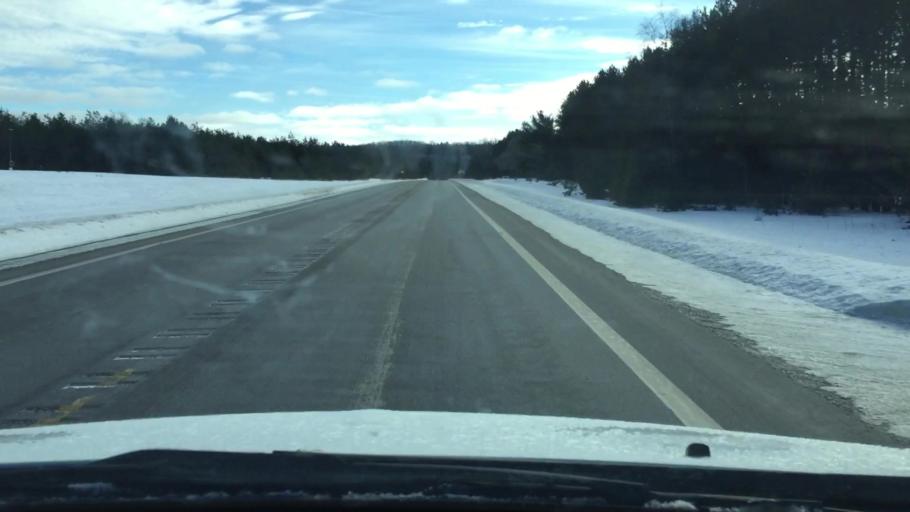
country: US
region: Michigan
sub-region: Antrim County
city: Mancelona
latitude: 44.9638
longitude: -85.0524
